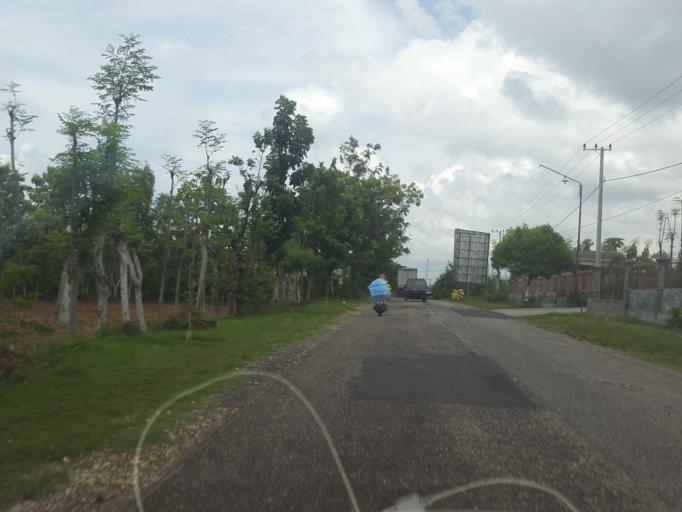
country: ID
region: East Java
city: Pesisir
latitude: -7.1176
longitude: 113.7639
